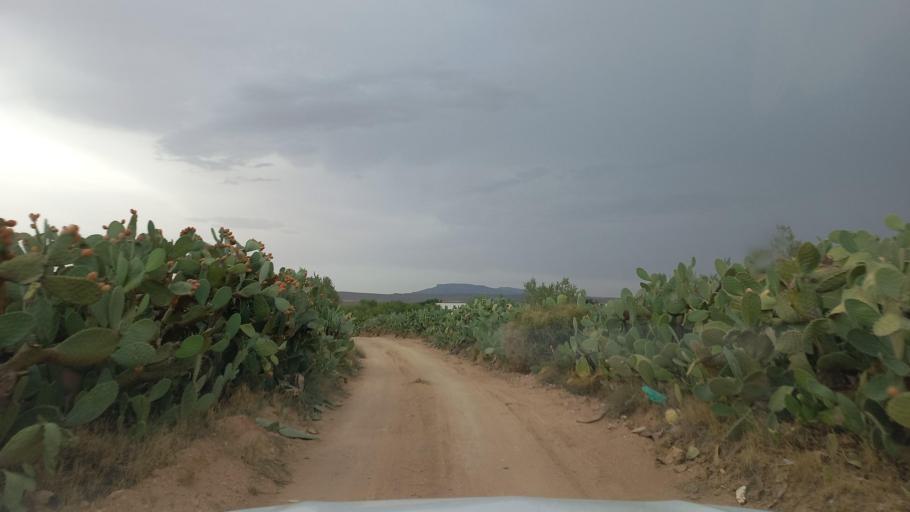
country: TN
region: Al Qasrayn
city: Kasserine
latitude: 35.2395
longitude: 9.0247
